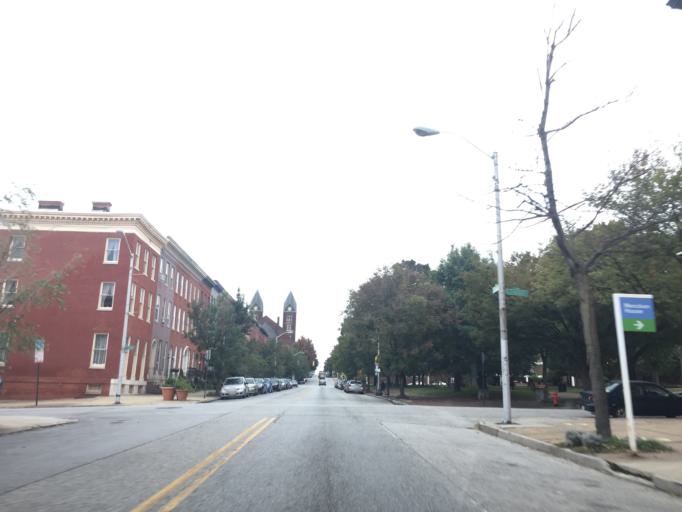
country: US
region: Maryland
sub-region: City of Baltimore
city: Baltimore
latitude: 39.2865
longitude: -76.6404
